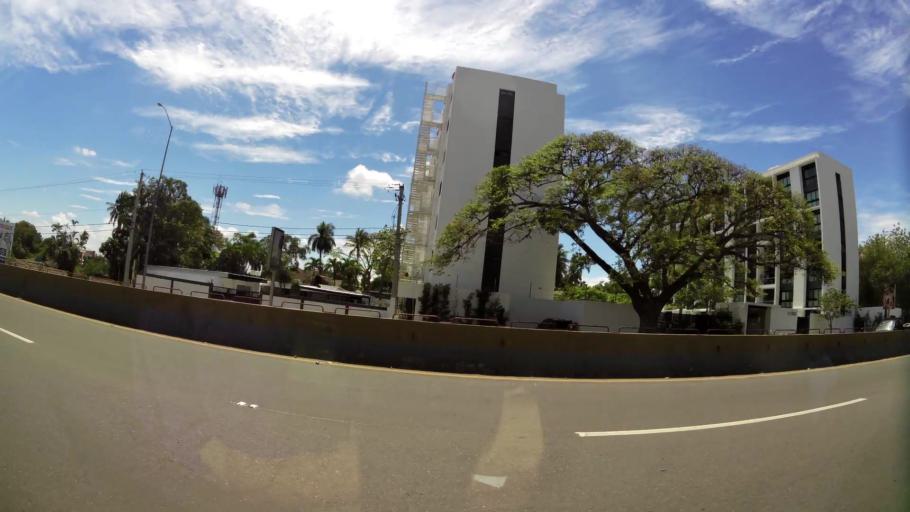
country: DO
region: Santiago
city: Santiago de los Caballeros
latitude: 19.4490
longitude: -70.6801
